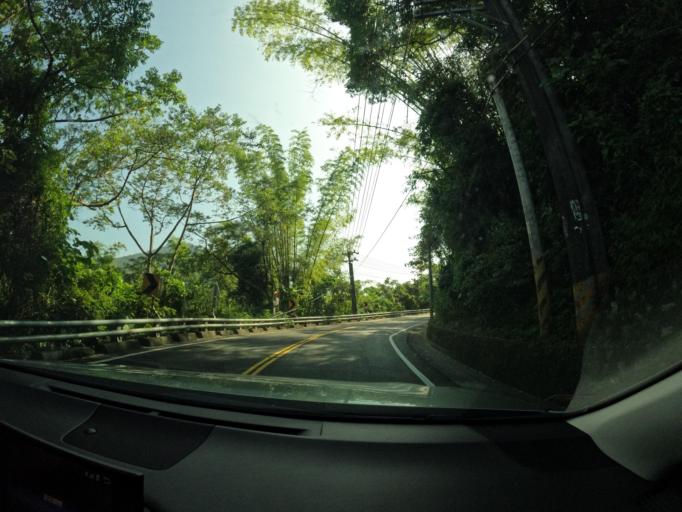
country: TW
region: Taiwan
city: Yujing
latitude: 23.0752
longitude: 120.6220
